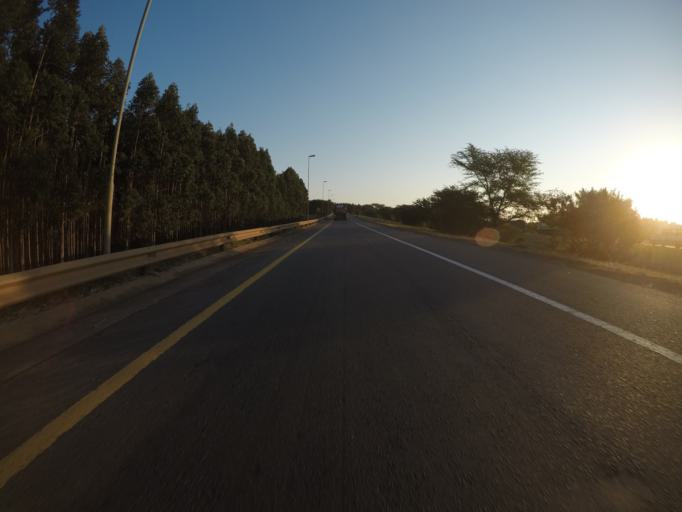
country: ZA
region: KwaZulu-Natal
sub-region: uThungulu District Municipality
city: Richards Bay
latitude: -28.6939
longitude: 32.0313
